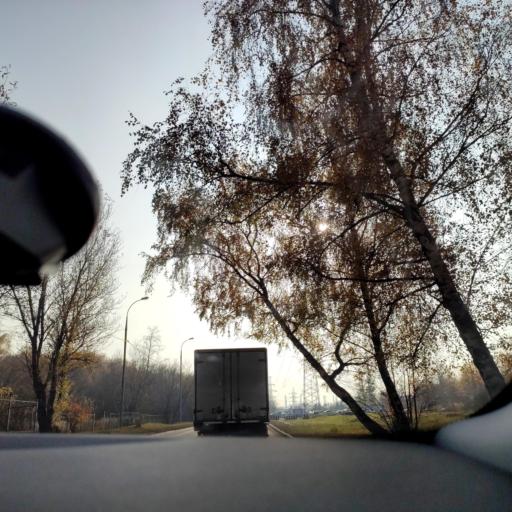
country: RU
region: Moscow
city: Kapotnya
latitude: 55.6642
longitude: 37.8090
